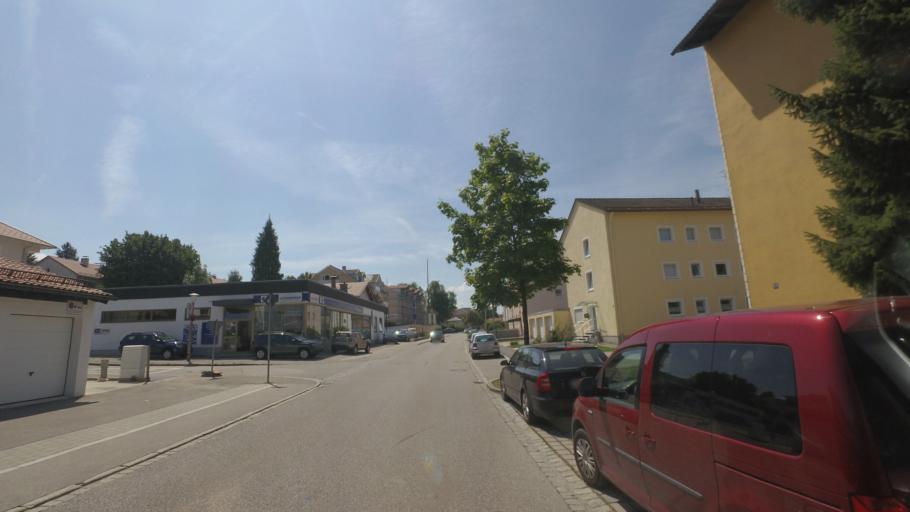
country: DE
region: Bavaria
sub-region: Upper Bavaria
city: Traunstein
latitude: 47.8770
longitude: 12.6346
